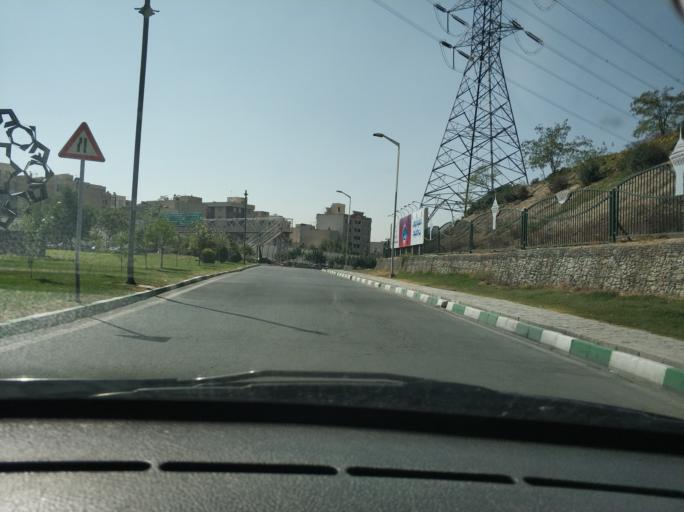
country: IR
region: Tehran
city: Tehran
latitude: 35.7424
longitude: 51.3773
